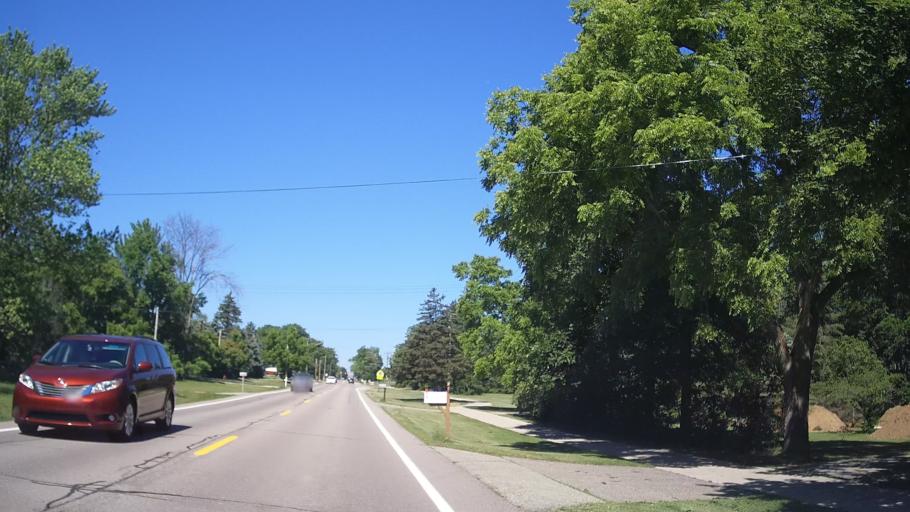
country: US
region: Michigan
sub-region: Oakland County
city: Troy
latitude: 42.6066
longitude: -83.1422
